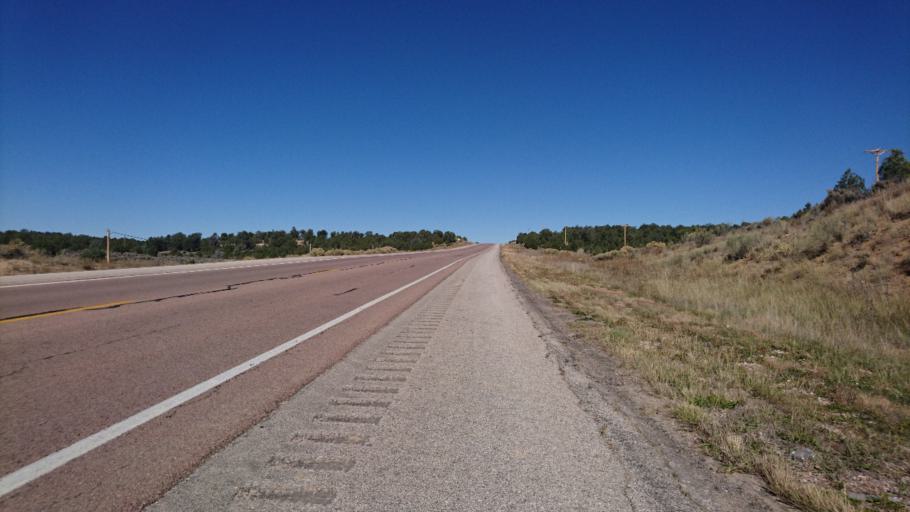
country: US
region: New Mexico
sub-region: McKinley County
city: Black Rock
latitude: 35.3040
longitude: -108.7575
